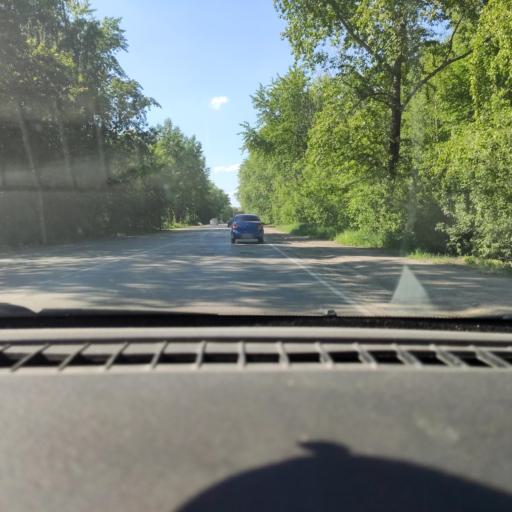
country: RU
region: Perm
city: Krasnokamsk
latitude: 58.0636
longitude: 55.8004
